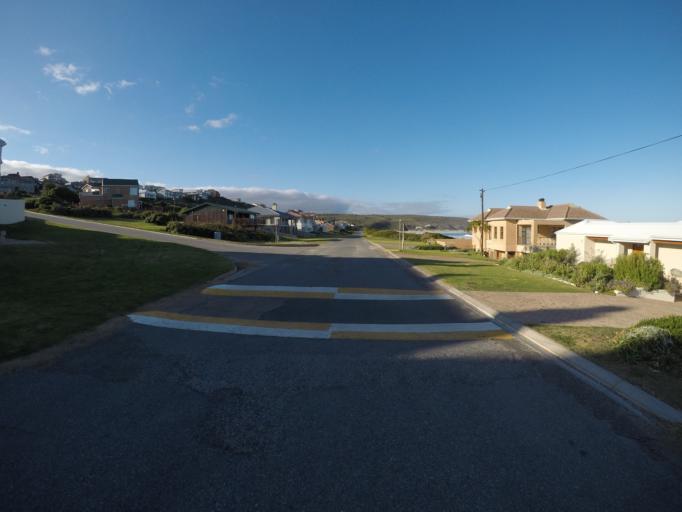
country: ZA
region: Western Cape
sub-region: Eden District Municipality
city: Riversdale
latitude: -34.4236
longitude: 21.3456
